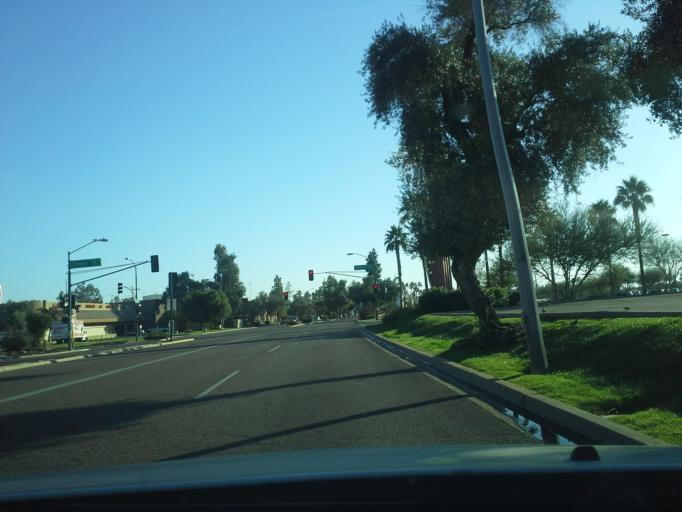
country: US
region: Arizona
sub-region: Maricopa County
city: Glendale
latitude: 33.5765
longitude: -112.1185
